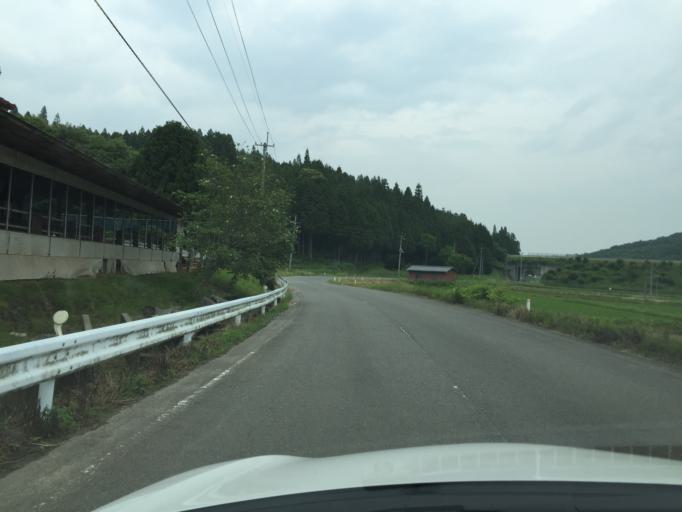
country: JP
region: Fukushima
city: Iwaki
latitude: 37.1779
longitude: 140.7143
